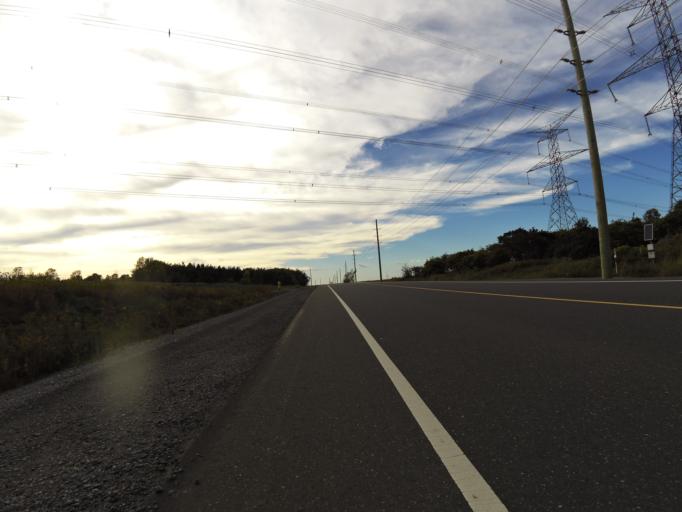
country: CA
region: Ontario
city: Oshawa
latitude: 43.8819
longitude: -78.7257
